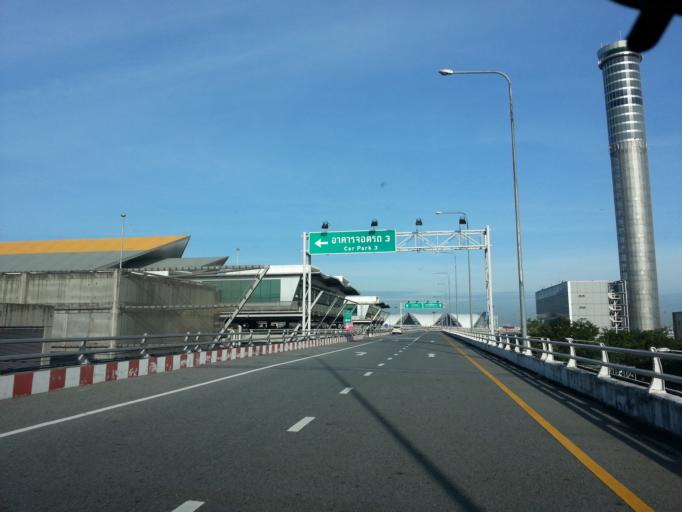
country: TH
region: Bangkok
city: Lat Krabang
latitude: 13.6952
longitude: 100.7516
